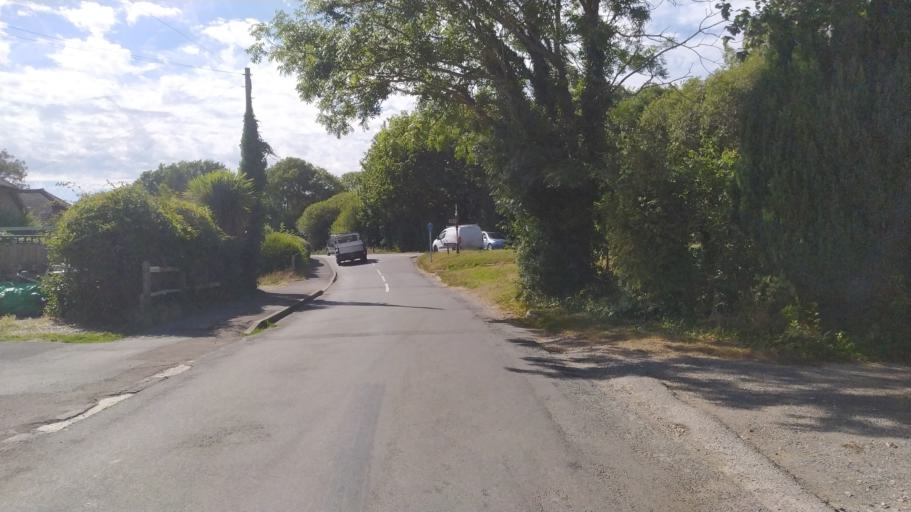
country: GB
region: England
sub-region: West Sussex
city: Chichester
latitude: 50.8142
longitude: -0.7597
